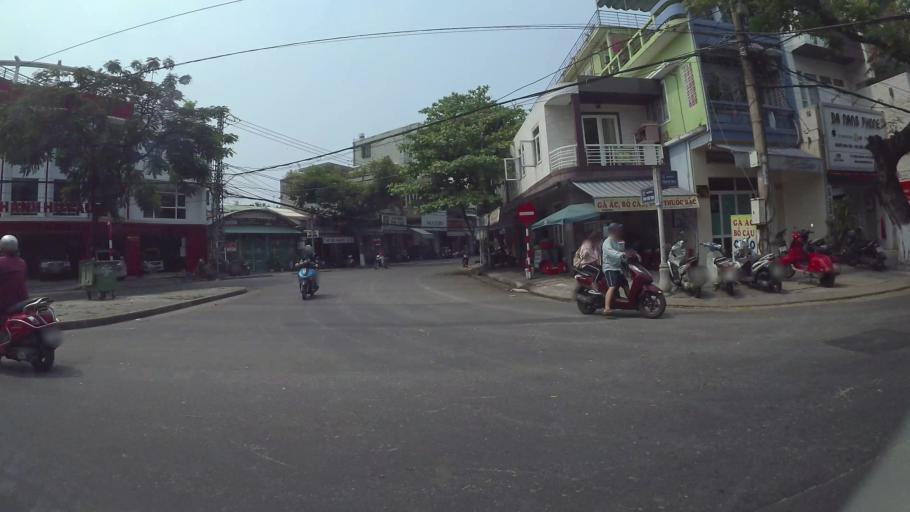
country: VN
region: Da Nang
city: Da Nang
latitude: 16.0539
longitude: 108.2192
